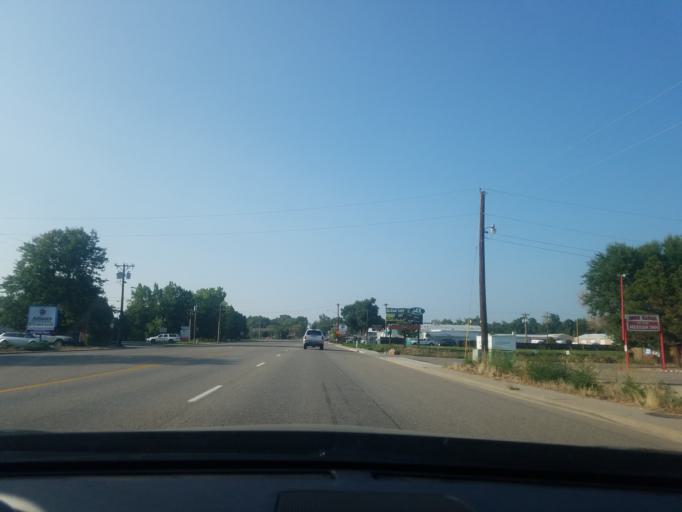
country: US
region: Colorado
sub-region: Larimer County
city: Loveland
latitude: 40.3845
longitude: -105.0733
